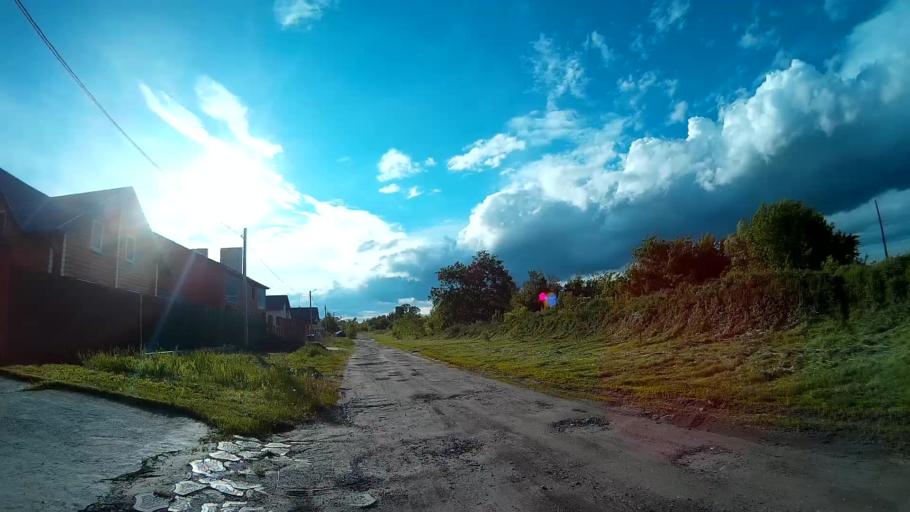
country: RU
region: Ulyanovsk
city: Novoul'yanovsk
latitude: 54.2042
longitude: 48.2734
